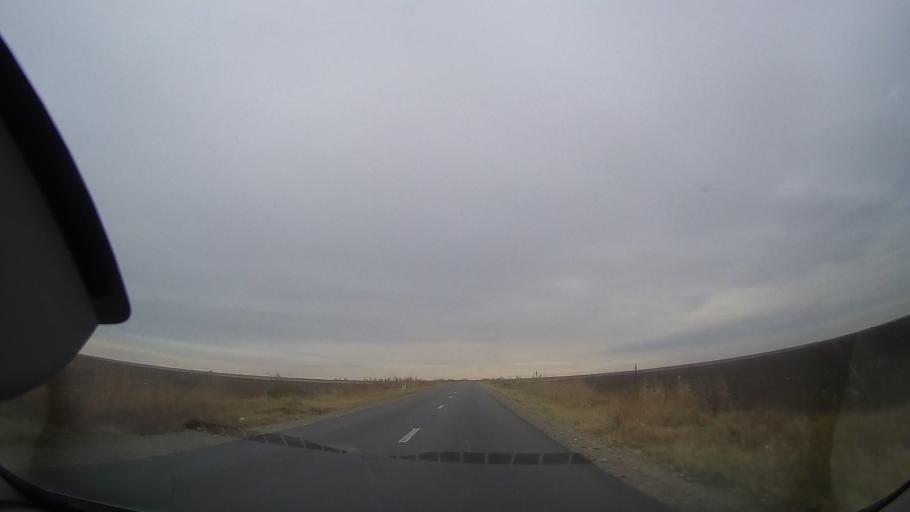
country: RO
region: Ialomita
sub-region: Oras Amara
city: Amara
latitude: 44.6429
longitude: 27.3006
